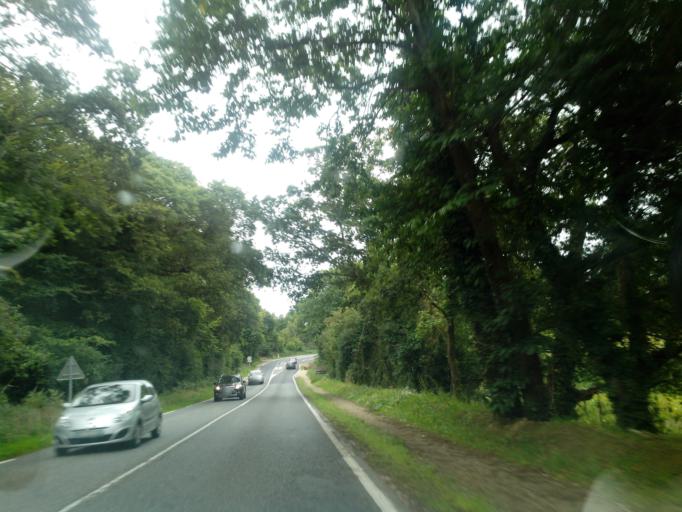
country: FR
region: Brittany
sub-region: Departement du Finistere
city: Quimperle
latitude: 47.8615
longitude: -3.5192
